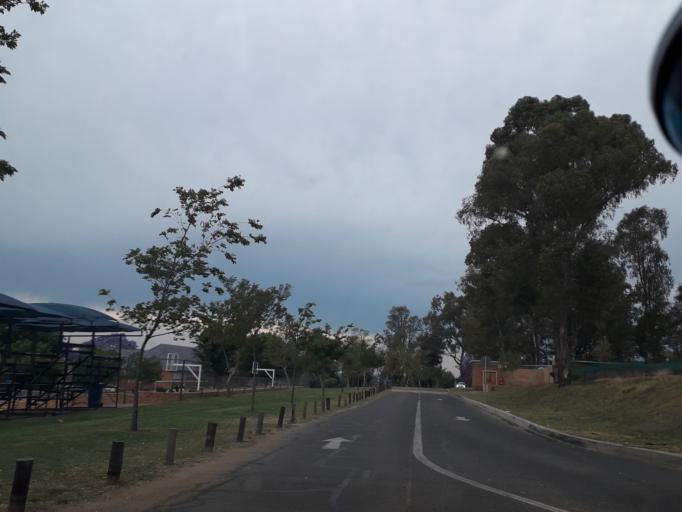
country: ZA
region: Gauteng
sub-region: City of Johannesburg Metropolitan Municipality
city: Johannesburg
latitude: -26.0886
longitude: 28.0145
